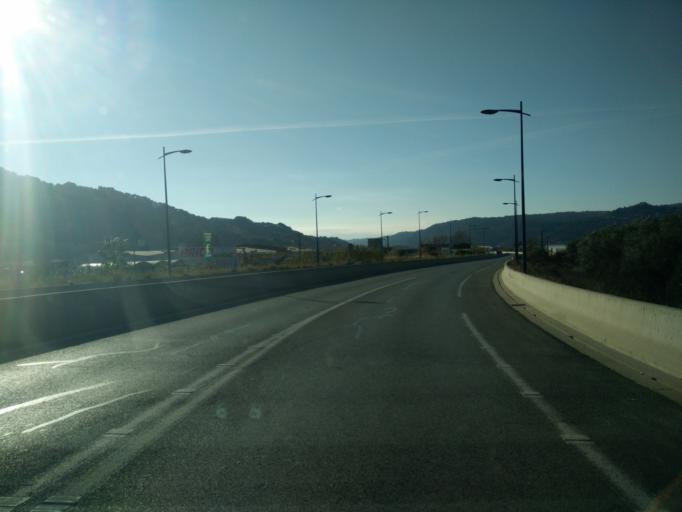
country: FR
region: Provence-Alpes-Cote d'Azur
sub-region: Departement des Alpes-Maritimes
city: Colomars
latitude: 43.7658
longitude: 7.2006
